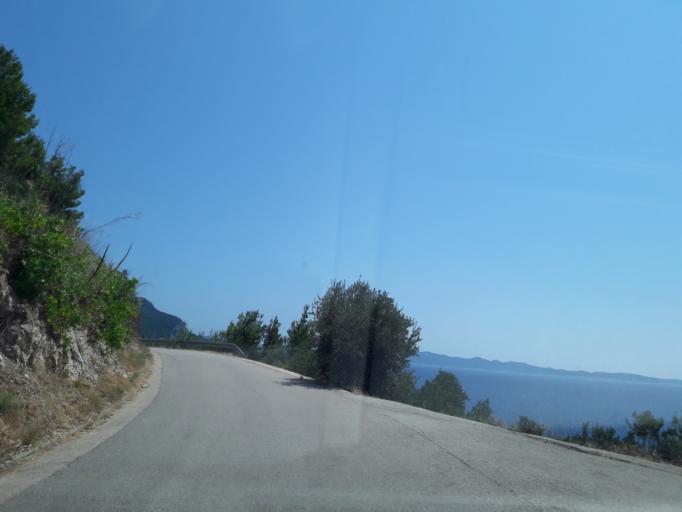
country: HR
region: Dubrovacko-Neretvanska
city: Blato
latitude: 42.9066
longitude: 17.4240
